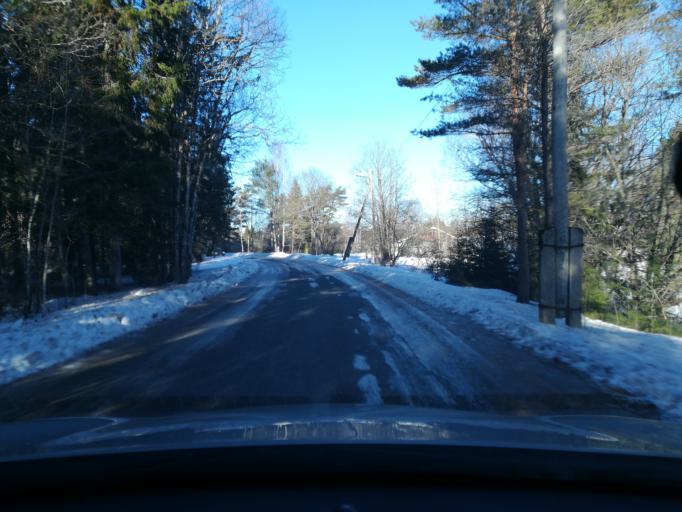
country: EE
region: Raplamaa
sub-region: Kohila vald
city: Kohila
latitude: 59.2285
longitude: 24.7515
